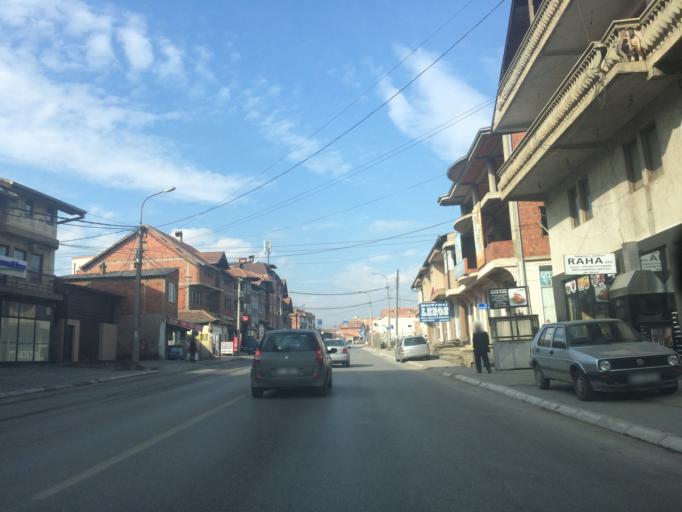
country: XK
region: Pristina
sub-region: Komuna e Prishtines
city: Pristina
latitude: 42.6803
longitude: 21.1601
